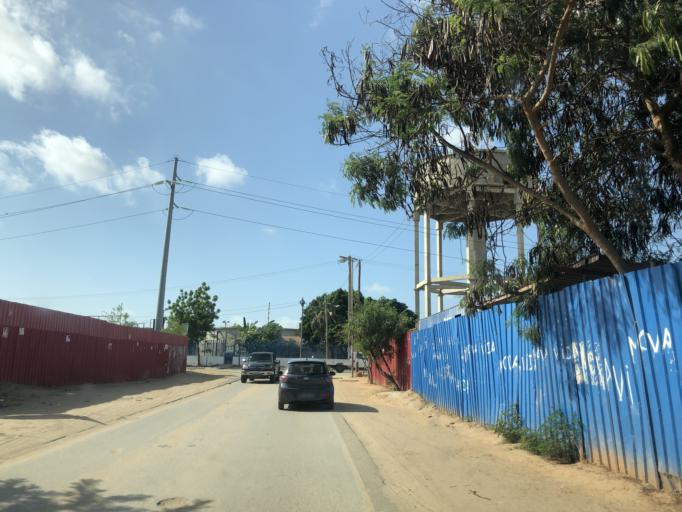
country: AO
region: Luanda
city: Luanda
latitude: -8.9075
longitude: 13.2326
